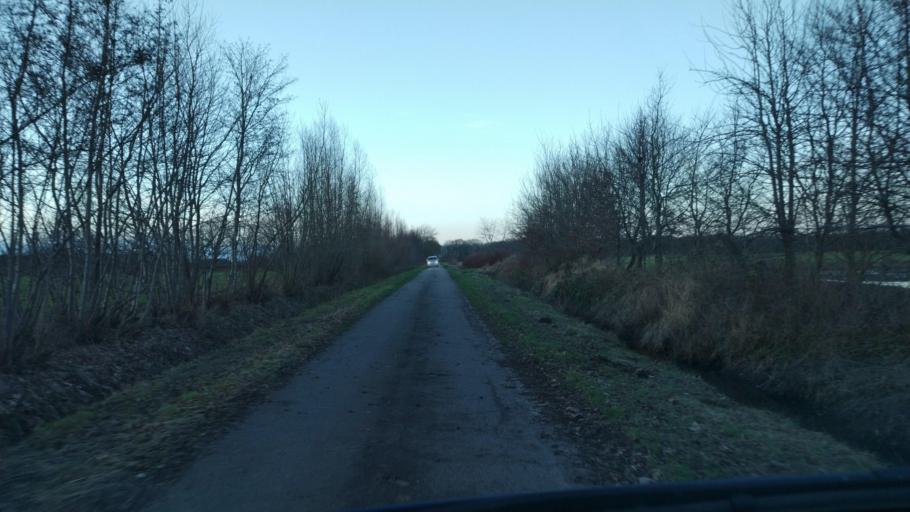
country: DE
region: Schleswig-Holstein
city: Dorpstedt
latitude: 54.4413
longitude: 9.3981
